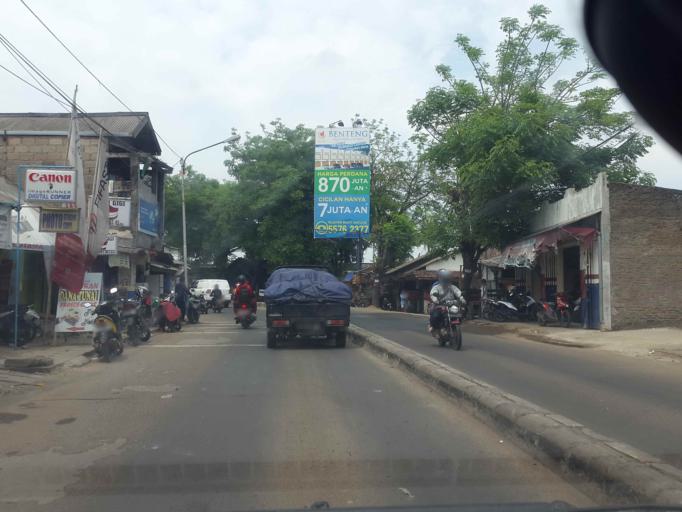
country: ID
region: Banten
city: Tangerang
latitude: -6.1615
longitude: 106.6440
